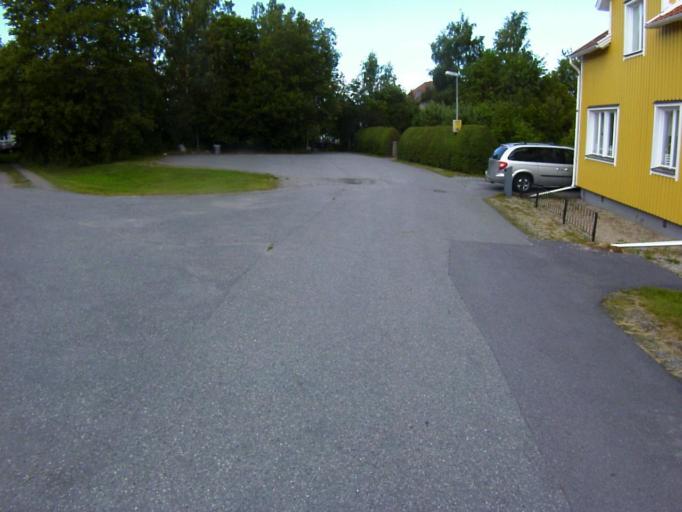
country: SE
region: Soedermanland
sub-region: Eskilstuna Kommun
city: Eskilstuna
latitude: 59.3738
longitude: 16.4771
